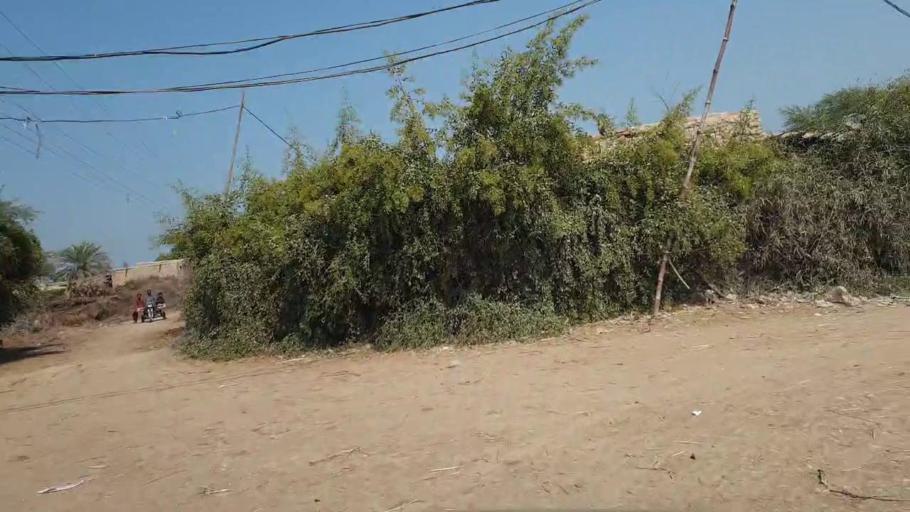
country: PK
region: Sindh
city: Hala
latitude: 25.9440
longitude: 68.4428
